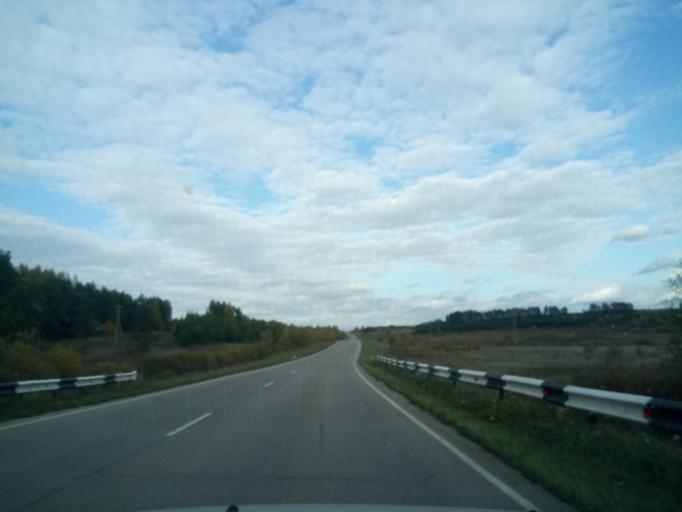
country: RU
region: Nizjnij Novgorod
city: Bol'shoye Boldino
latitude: 54.9101
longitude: 45.1173
